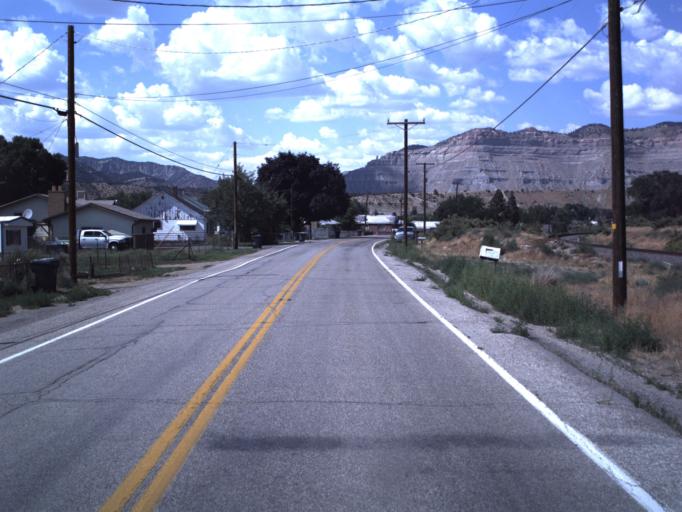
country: US
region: Utah
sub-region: Carbon County
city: Spring Glen
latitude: 39.6603
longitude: -110.8565
